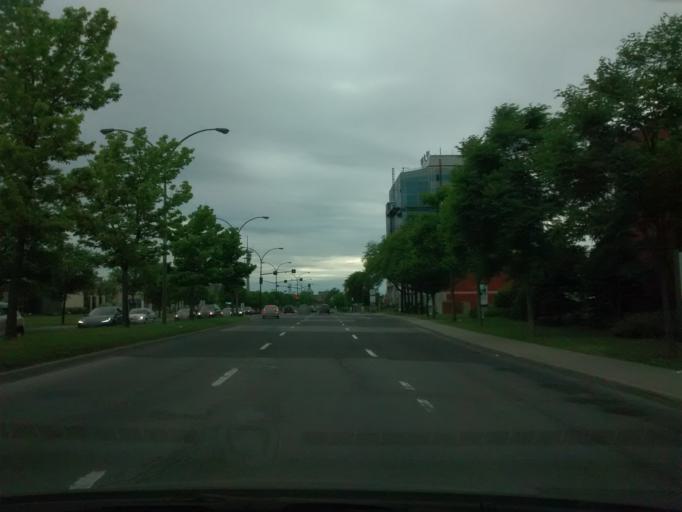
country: CA
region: Quebec
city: Mont-Royal
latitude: 45.5319
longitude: -73.6517
